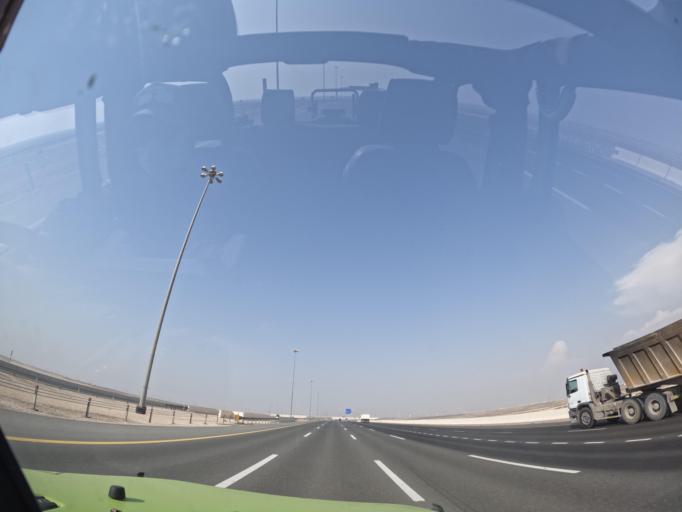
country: AE
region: Dubai
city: Dubai
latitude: 24.8428
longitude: 55.0023
